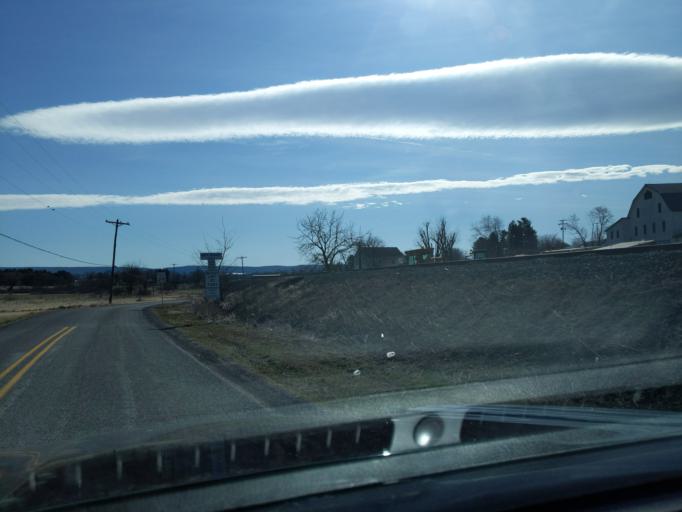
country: US
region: Pennsylvania
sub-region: Blair County
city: Martinsburg
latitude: 40.3123
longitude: -78.3439
